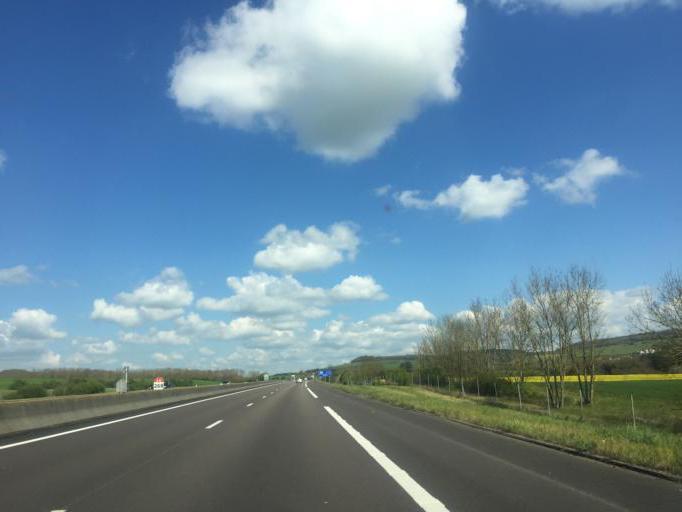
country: FR
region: Bourgogne
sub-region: Departement de la Cote-d'Or
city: Pouilly-en-Auxois
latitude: 47.2287
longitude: 4.5870
